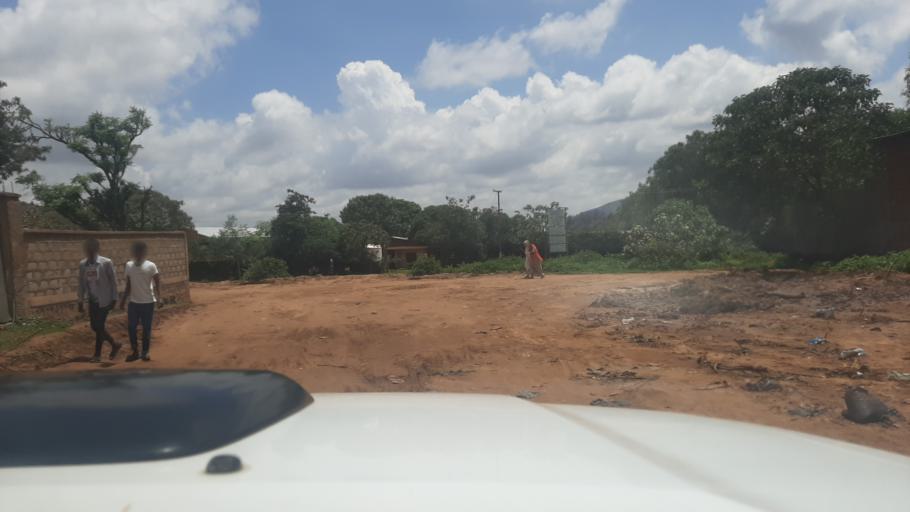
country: ET
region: Oromiya
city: Yabelo
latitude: 4.8952
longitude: 38.0977
